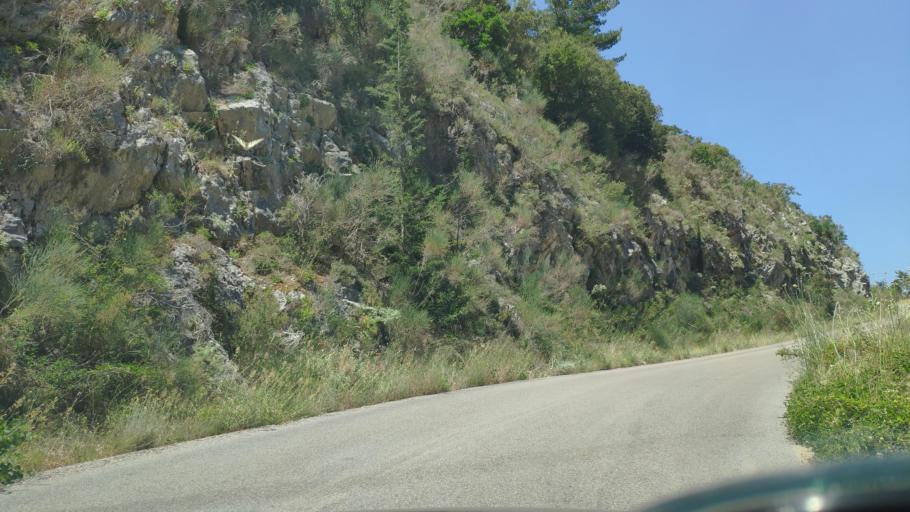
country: GR
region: Ionian Islands
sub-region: Lefkada
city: Nidri
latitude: 38.7436
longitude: 20.6214
